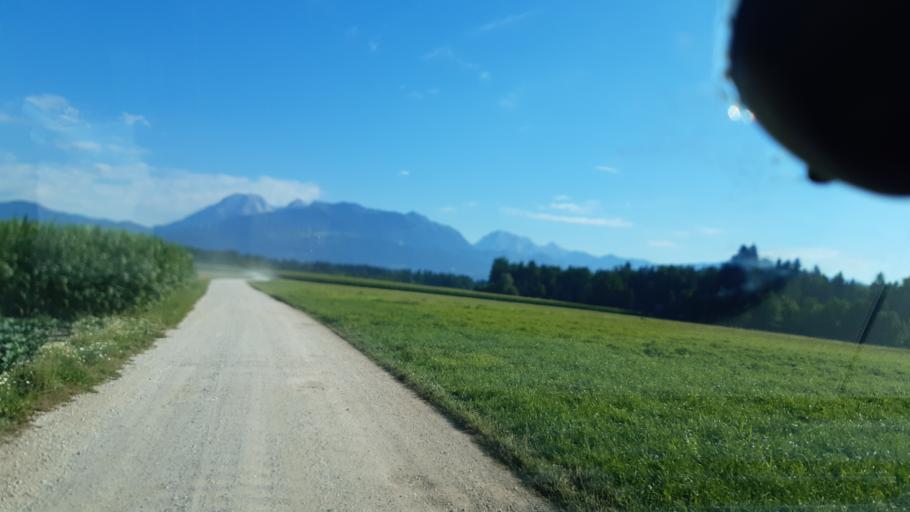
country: SI
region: Vodice
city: Vodice
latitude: 46.1850
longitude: 14.5078
